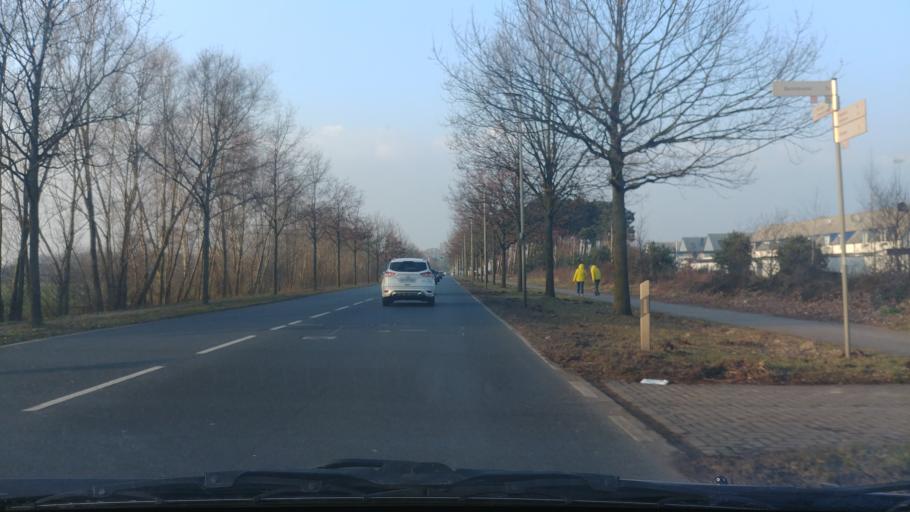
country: DE
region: Lower Saxony
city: Garbsen-Mitte
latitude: 52.4277
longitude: 9.6475
